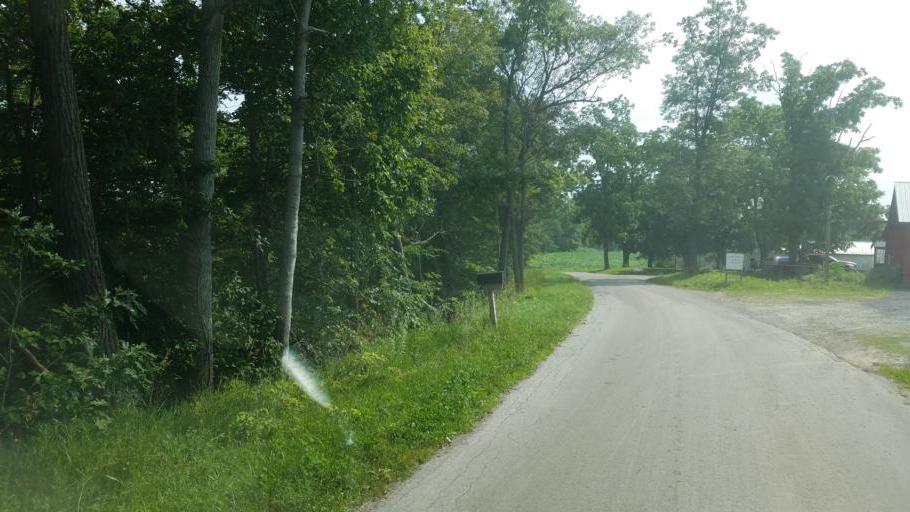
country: US
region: Ohio
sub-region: Hardin County
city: Kenton
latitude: 40.6183
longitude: -83.5197
